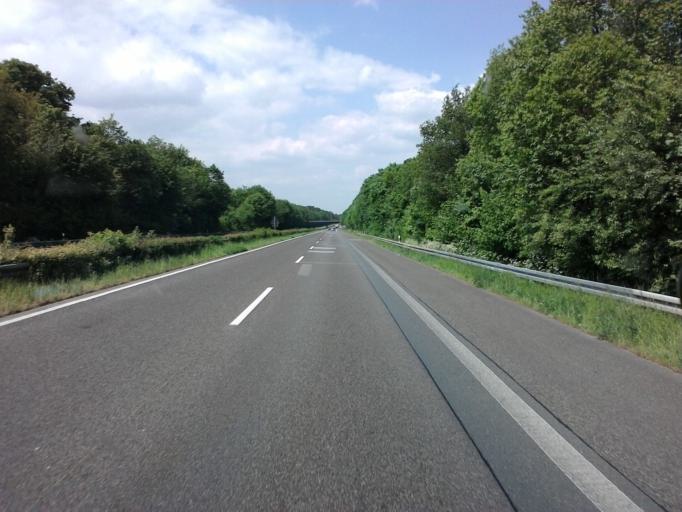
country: DE
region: North Rhine-Westphalia
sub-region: Regierungsbezirk Dusseldorf
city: Sonsbeck
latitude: 51.5842
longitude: 6.3929
